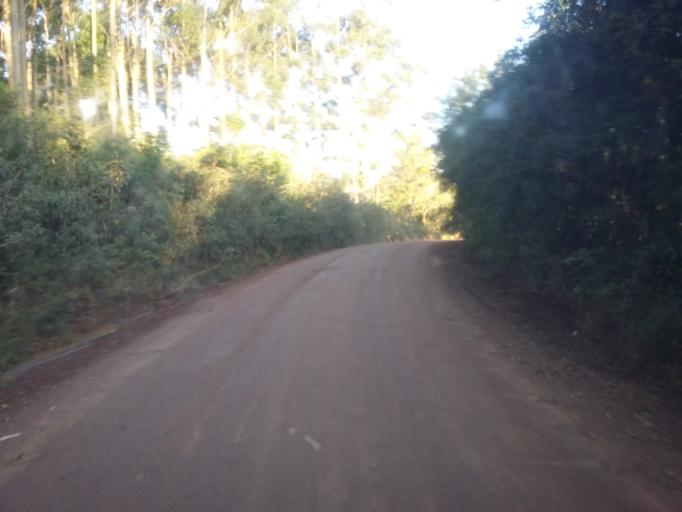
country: BR
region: Rio Grande do Sul
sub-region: Camaqua
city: Camaqua
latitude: -30.7074
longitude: -51.7676
